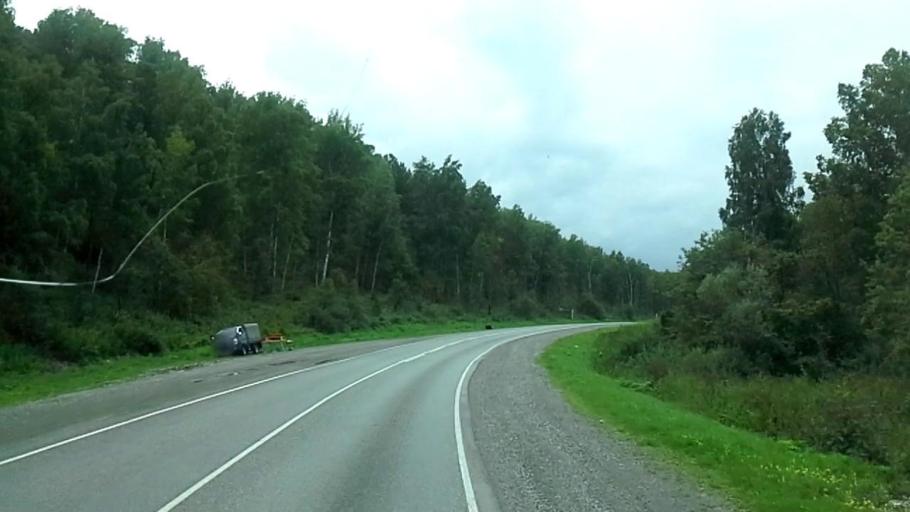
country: RU
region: Altay
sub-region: Mayminskiy Rayon
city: Manzherok
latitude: 51.8596
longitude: 85.7587
